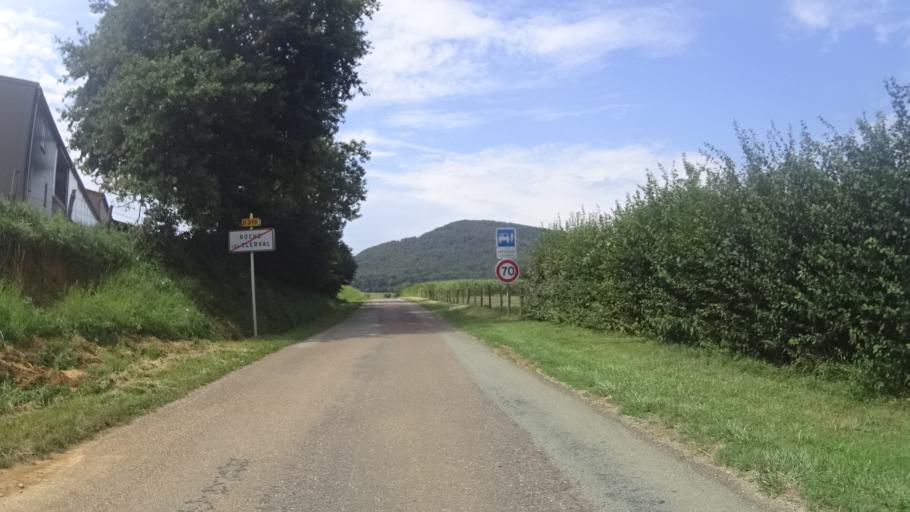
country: FR
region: Franche-Comte
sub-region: Departement du Doubs
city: Clerval
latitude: 47.3676
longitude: 6.4732
